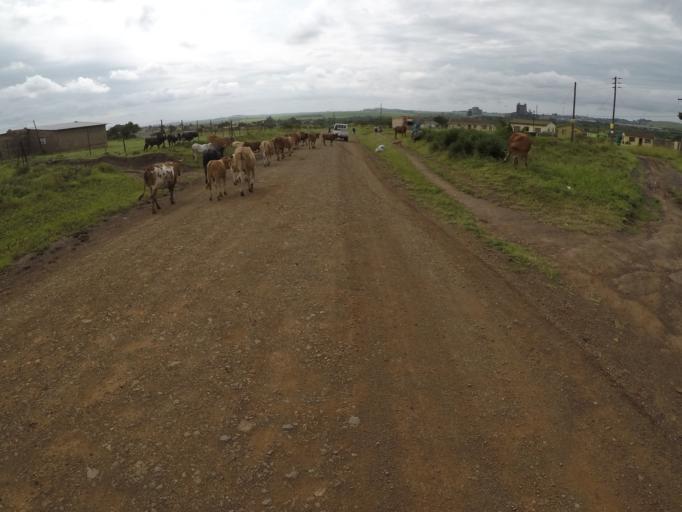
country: ZA
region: KwaZulu-Natal
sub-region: uThungulu District Municipality
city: Empangeni
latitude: -28.7124
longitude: 31.8571
